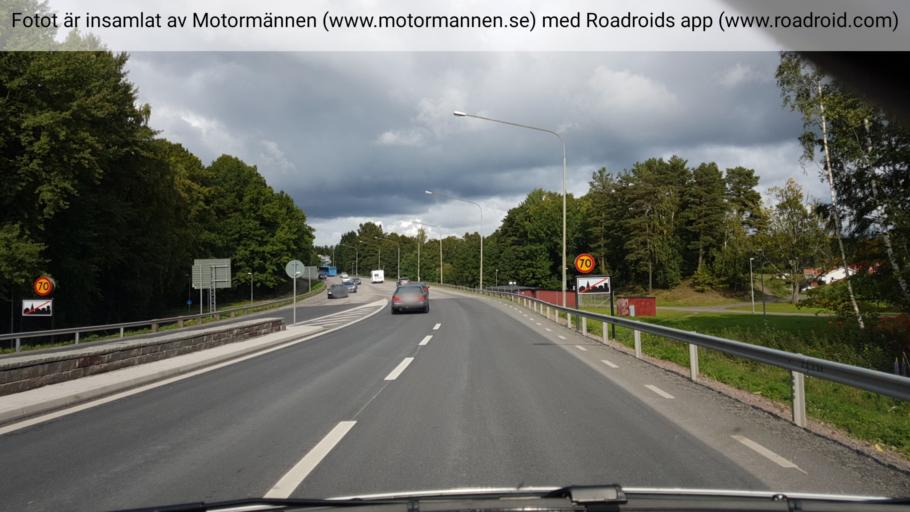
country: SE
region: Vaestra Goetaland
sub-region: Skovde Kommun
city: Skoevde
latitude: 58.4145
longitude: 13.8680
